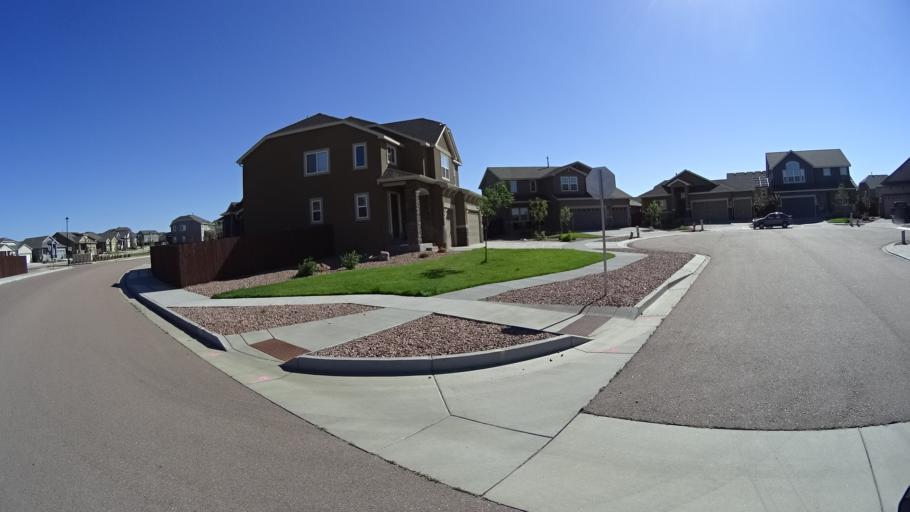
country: US
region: Colorado
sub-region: El Paso County
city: Black Forest
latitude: 38.9473
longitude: -104.6761
